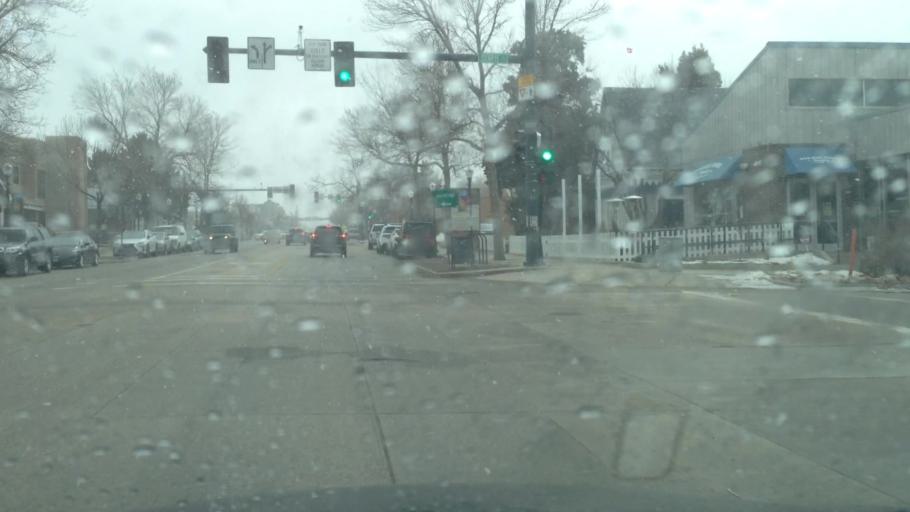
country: US
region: Colorado
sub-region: Douglas County
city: Castle Rock
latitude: 39.3756
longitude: -104.8600
